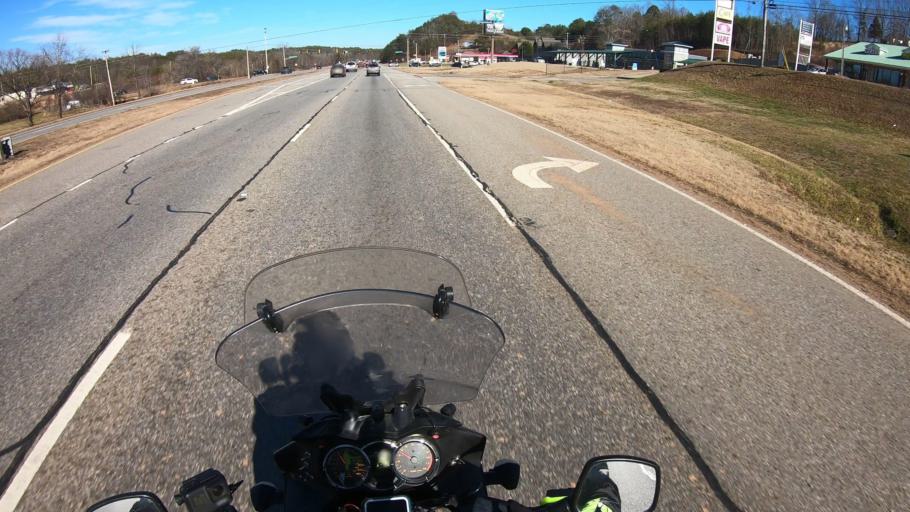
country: US
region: Georgia
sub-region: Fannin County
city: Blue Ridge
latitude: 34.8805
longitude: -84.2939
